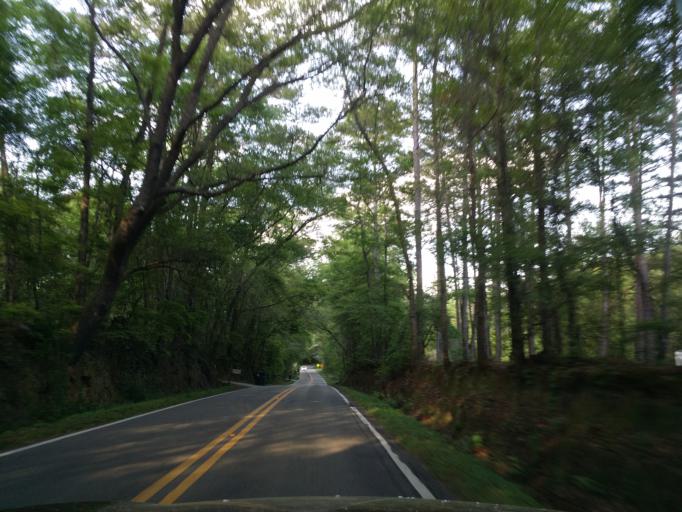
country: US
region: Florida
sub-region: Leon County
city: Tallahassee
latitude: 30.5201
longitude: -84.1242
